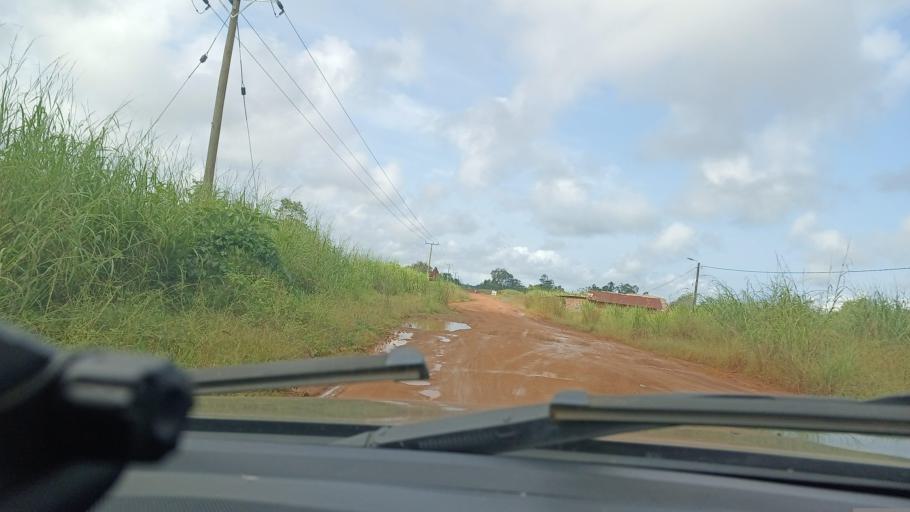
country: LR
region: Grand Cape Mount
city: Robertsport
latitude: 6.6868
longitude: -11.1206
